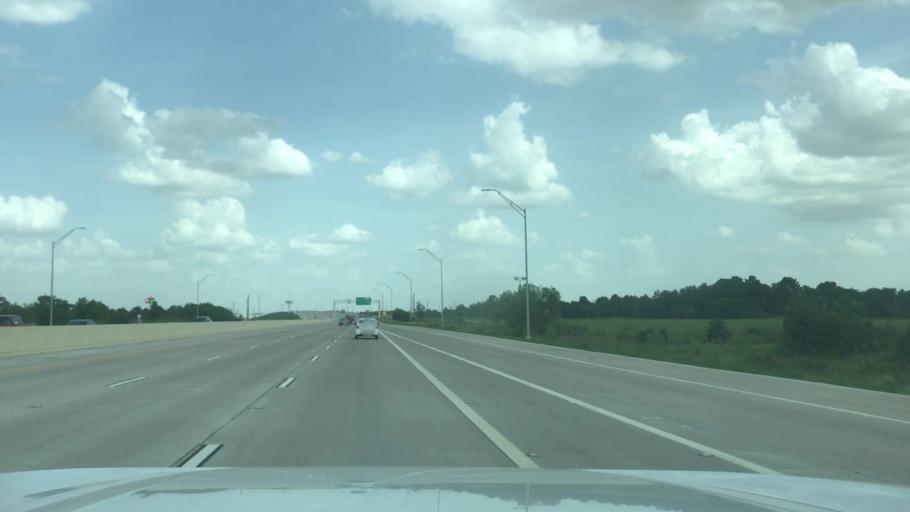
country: US
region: Texas
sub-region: Waller County
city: Waller
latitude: 30.0667
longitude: -95.9169
